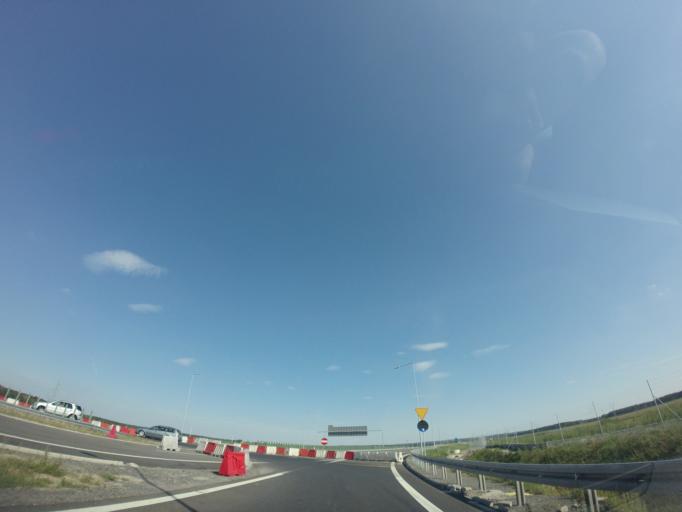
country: PL
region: Lubusz
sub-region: Powiat nowosolski
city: Nowe Miasteczko
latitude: 51.7276
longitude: 15.7316
